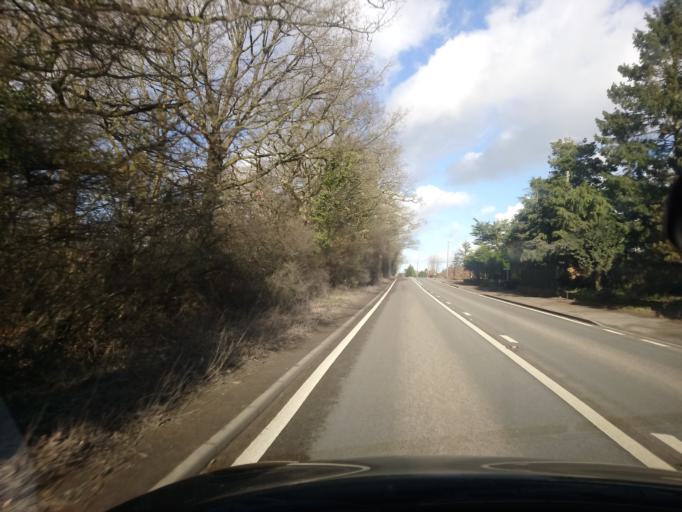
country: GB
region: England
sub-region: Shropshire
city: Astley
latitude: 52.7566
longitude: -2.7164
